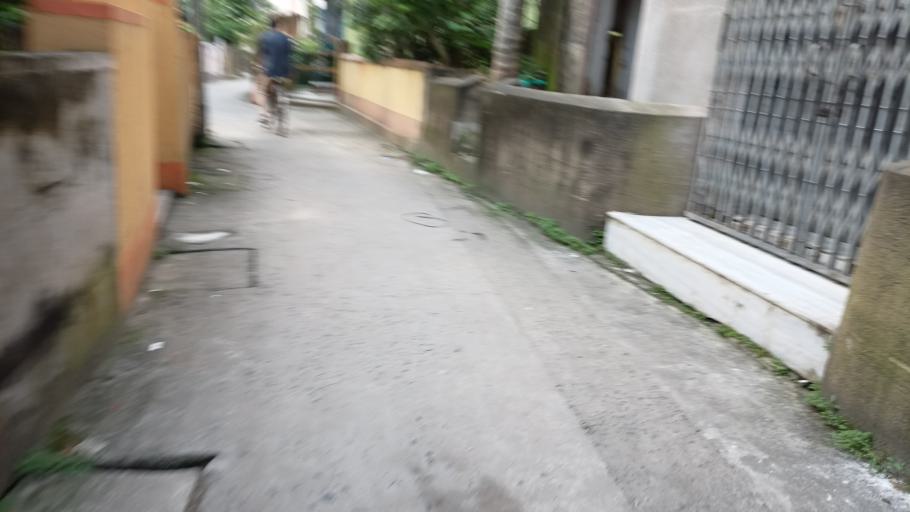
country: IN
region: West Bengal
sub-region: North 24 Parganas
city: Bangaon
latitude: 23.0487
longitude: 88.8256
